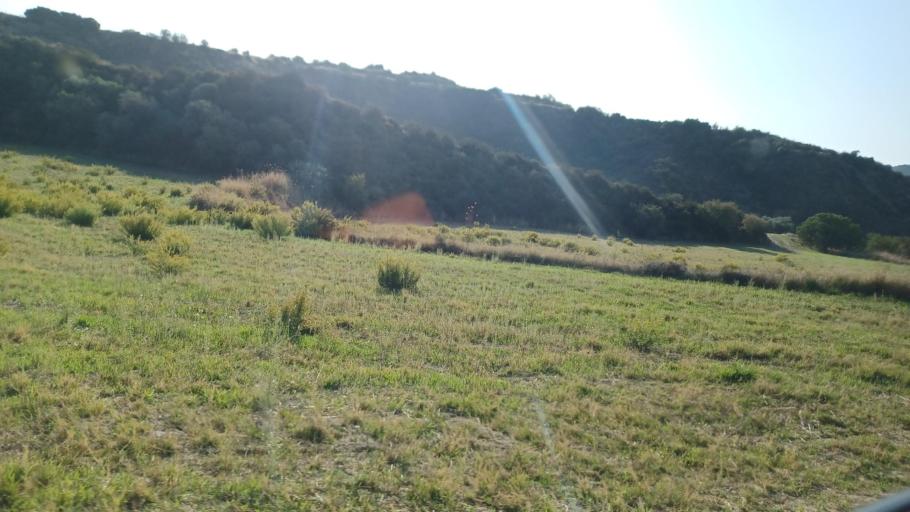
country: CY
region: Pafos
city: Polis
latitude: 35.0040
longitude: 32.4572
